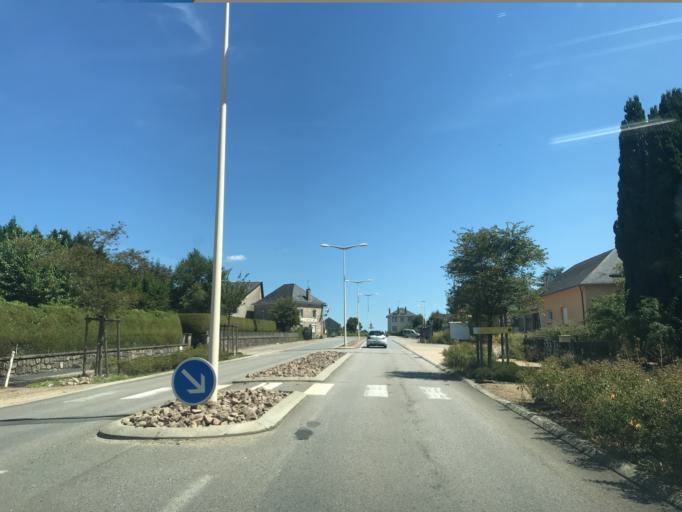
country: FR
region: Limousin
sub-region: Departement de la Correze
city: Correze
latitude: 45.3316
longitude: 1.8777
